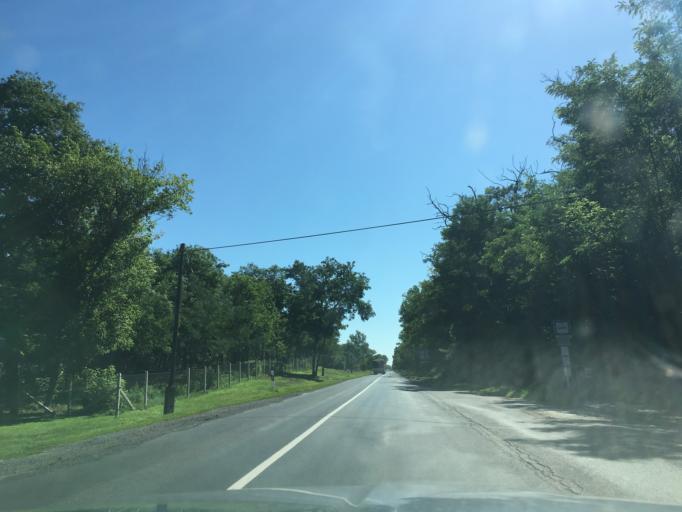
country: HU
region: Hajdu-Bihar
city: Hajdusamson
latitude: 47.5257
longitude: 21.7752
